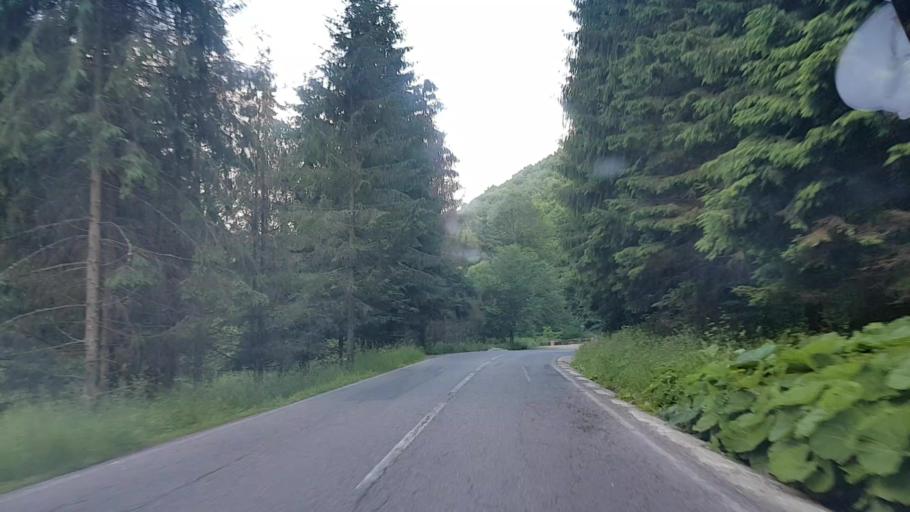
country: RO
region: Harghita
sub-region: Comuna Praid
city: Ocna de Sus
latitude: 46.5986
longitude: 25.2396
